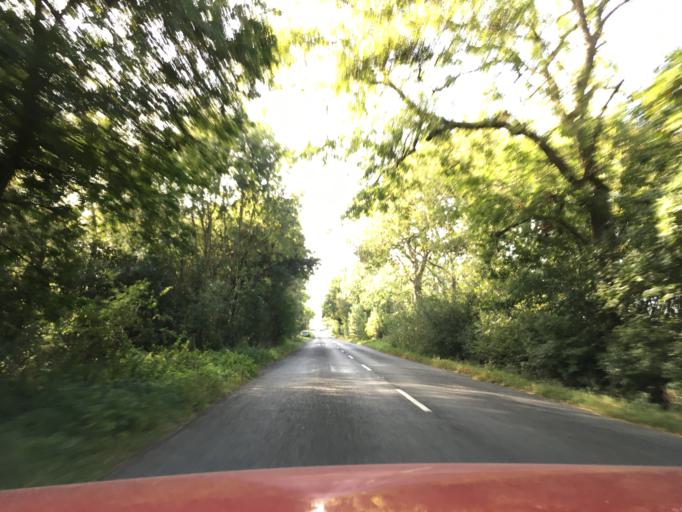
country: GB
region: England
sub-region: Gloucestershire
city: Tewkesbury
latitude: 51.9477
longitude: -2.2216
